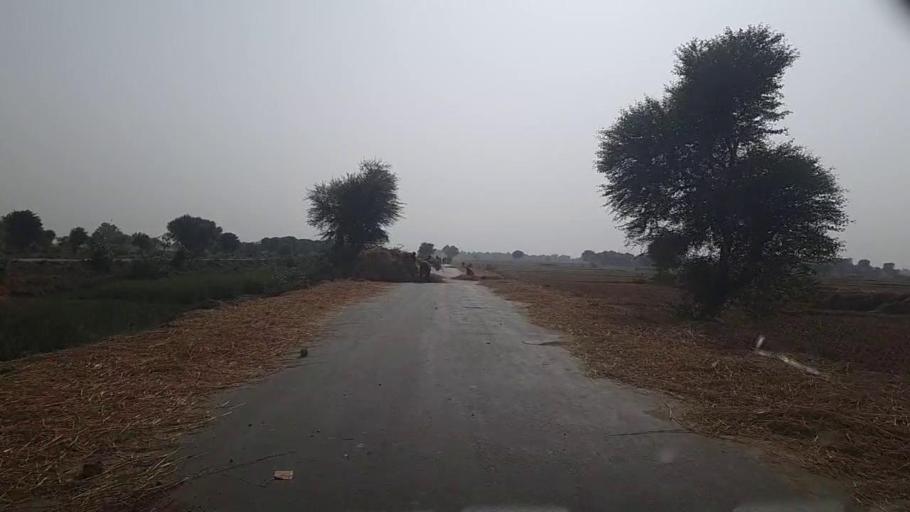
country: PK
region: Sindh
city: Kashmor
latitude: 28.4182
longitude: 69.5694
